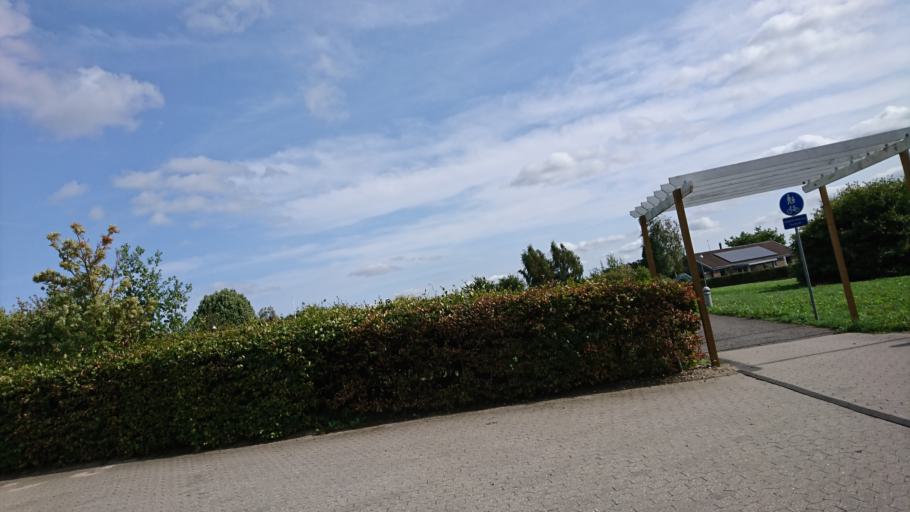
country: DK
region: Capital Region
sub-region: Egedal Kommune
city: Smorumnedre
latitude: 55.7466
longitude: 12.2961
